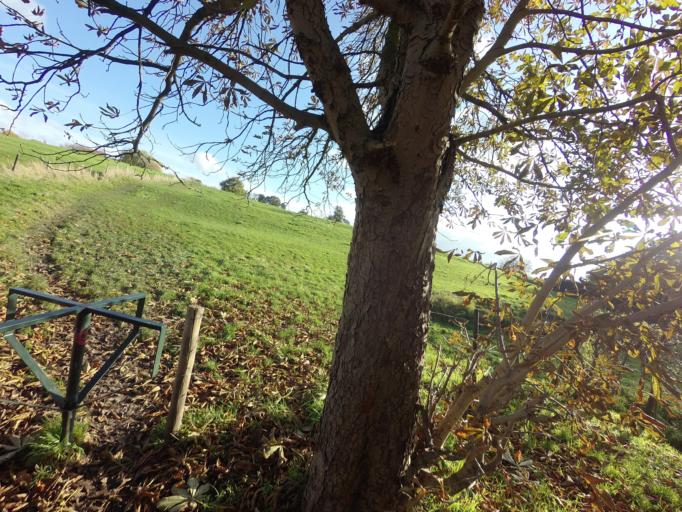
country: BE
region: Wallonia
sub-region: Province de Liege
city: Plombieres
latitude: 50.7612
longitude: 5.9122
